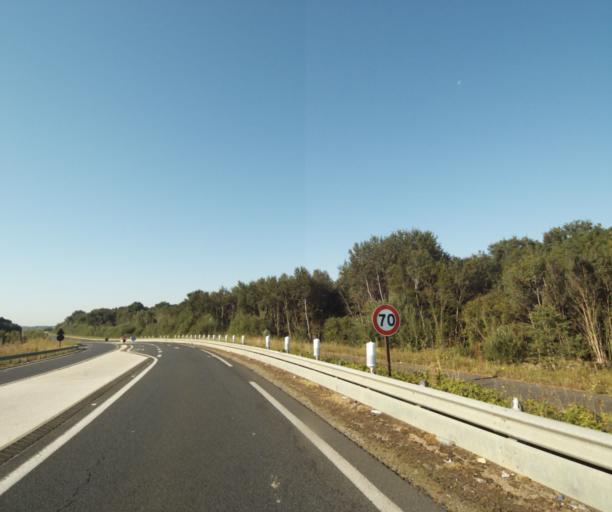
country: FR
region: Ile-de-France
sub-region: Departement de Seine-et-Marne
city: Moissy-Cramayel
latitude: 48.5978
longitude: 2.6043
